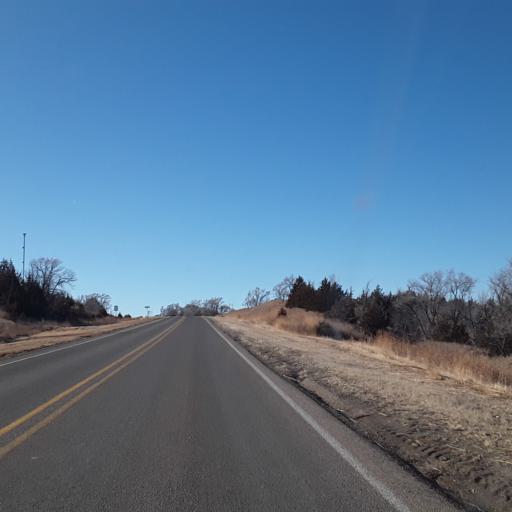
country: US
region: Nebraska
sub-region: Frontier County
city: Stockville
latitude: 40.6576
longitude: -100.6264
